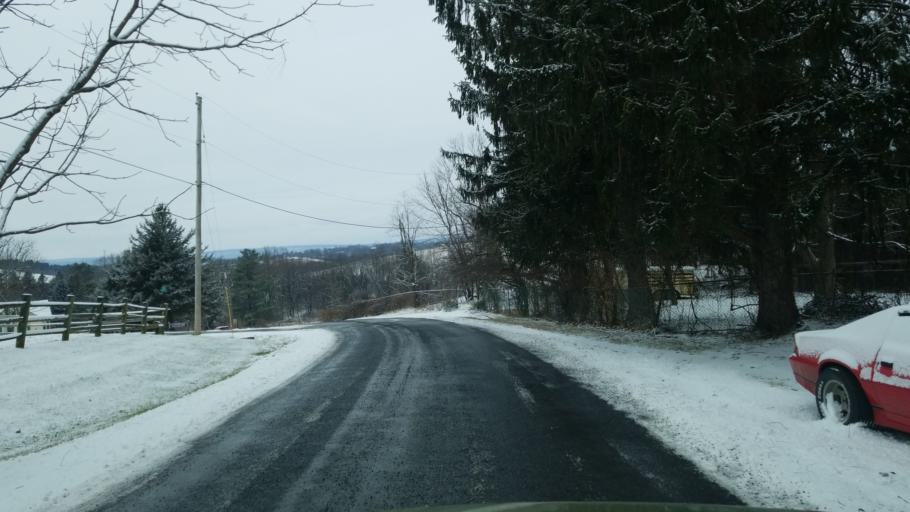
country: US
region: Pennsylvania
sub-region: Centre County
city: Centre Hall
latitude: 40.7783
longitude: -77.6720
